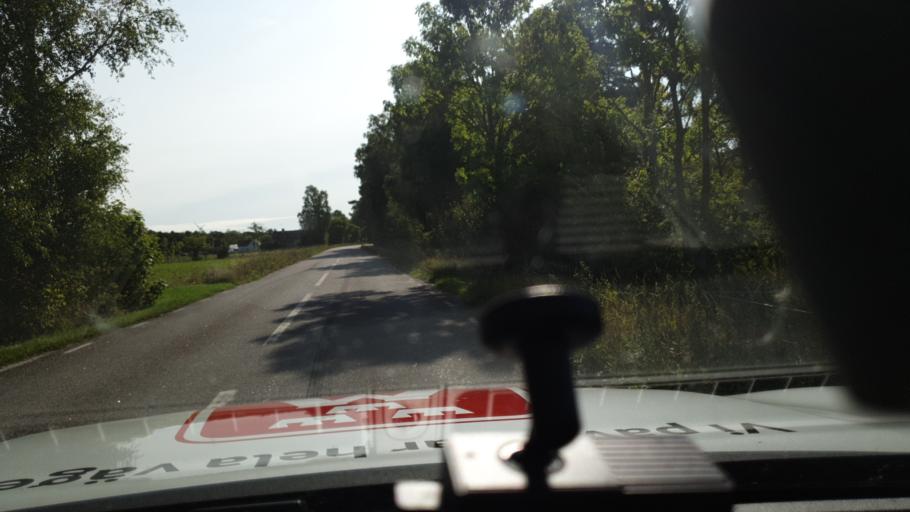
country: SE
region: Gotland
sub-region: Gotland
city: Hemse
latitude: 57.1108
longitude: 18.2881
